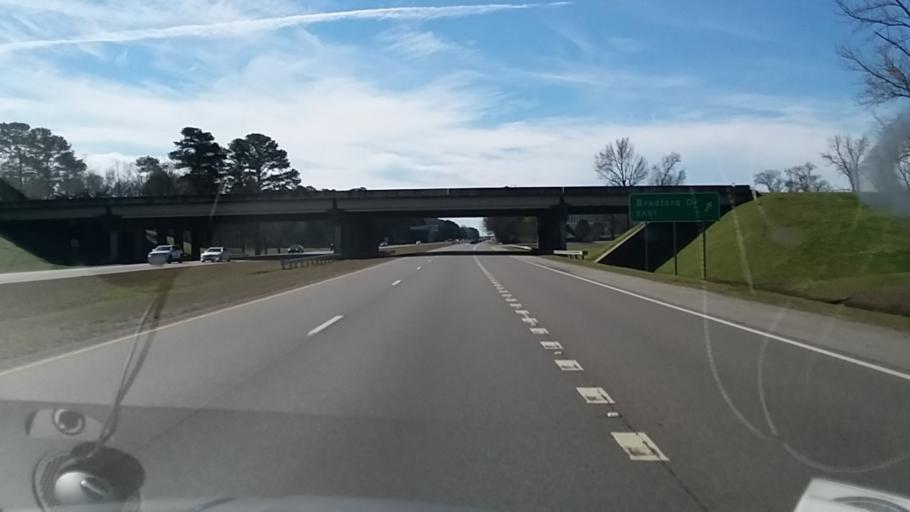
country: US
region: Alabama
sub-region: Madison County
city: Redstone Arsenal
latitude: 34.7290
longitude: -86.6704
